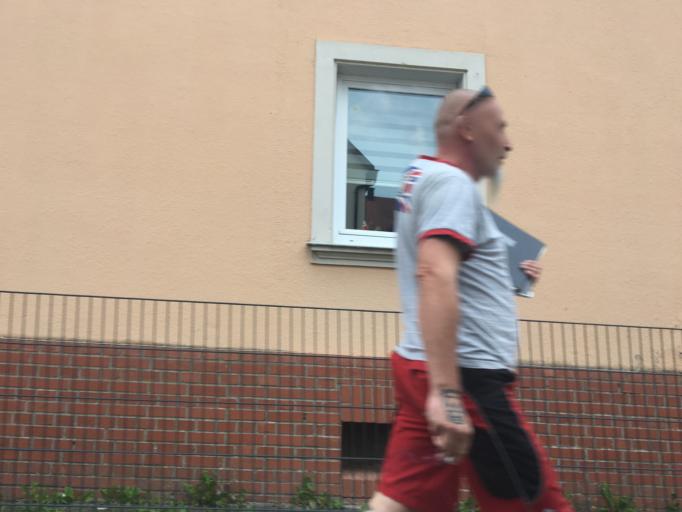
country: DE
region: Bavaria
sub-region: Regierungsbezirk Mittelfranken
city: Wilhermsdorf
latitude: 49.4828
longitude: 10.7118
